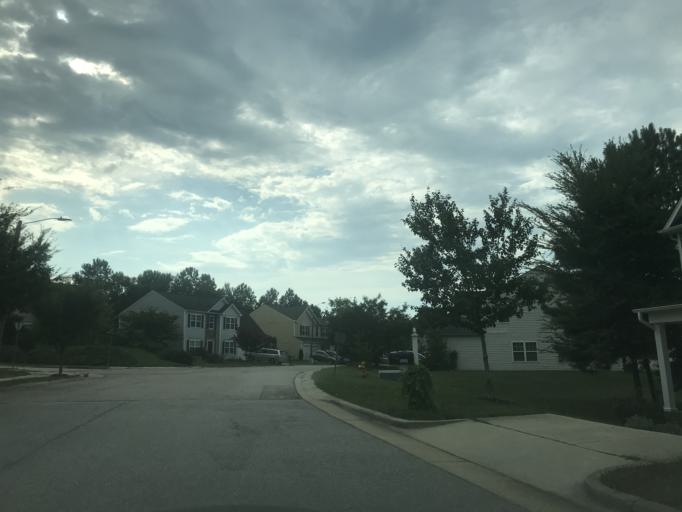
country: US
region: North Carolina
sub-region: Wake County
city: Knightdale
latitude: 35.8415
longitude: -78.5570
